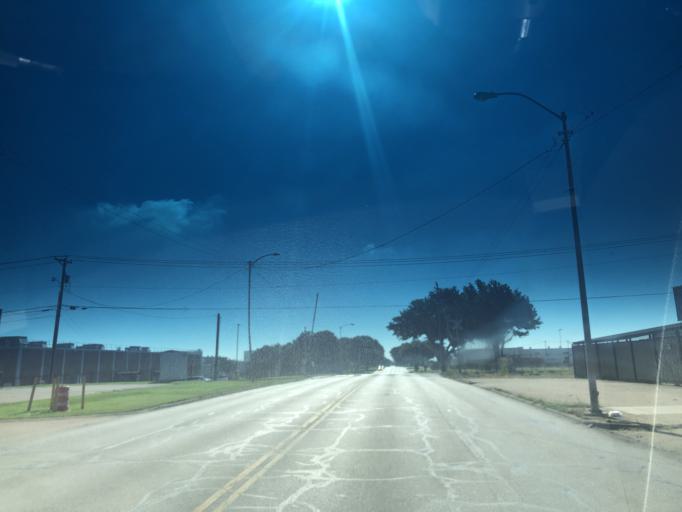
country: US
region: Texas
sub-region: Dallas County
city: Grand Prairie
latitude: 32.7206
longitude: -97.0425
